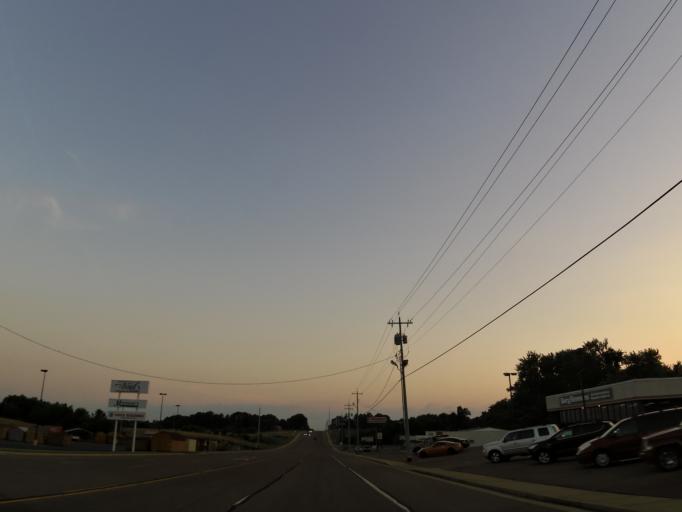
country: US
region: Tennessee
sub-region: Carroll County
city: McKenzie
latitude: 36.1194
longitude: -88.5222
